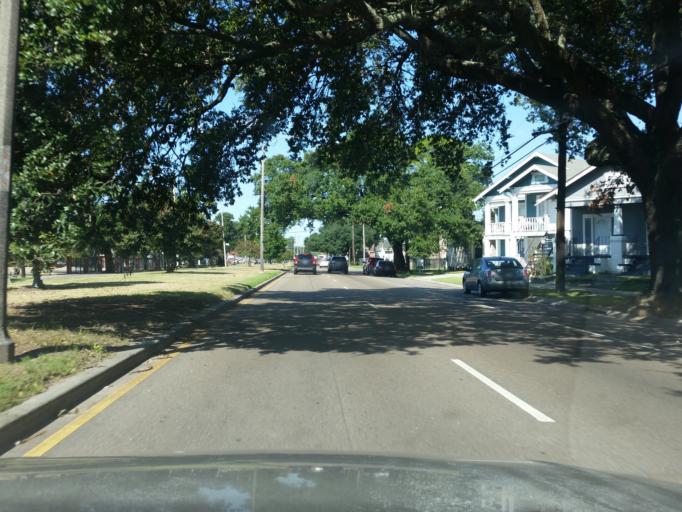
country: US
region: Louisiana
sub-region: Orleans Parish
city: New Orleans
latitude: 29.9855
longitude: -90.0697
